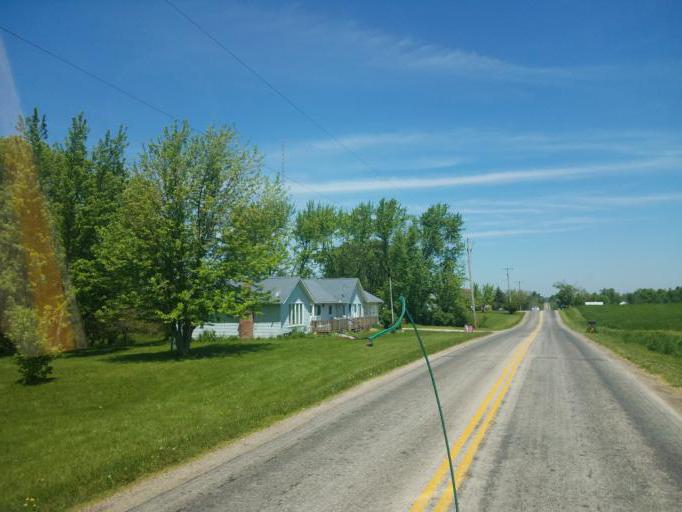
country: US
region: Ohio
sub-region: Ashland County
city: Ashland
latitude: 40.9389
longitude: -82.2435
